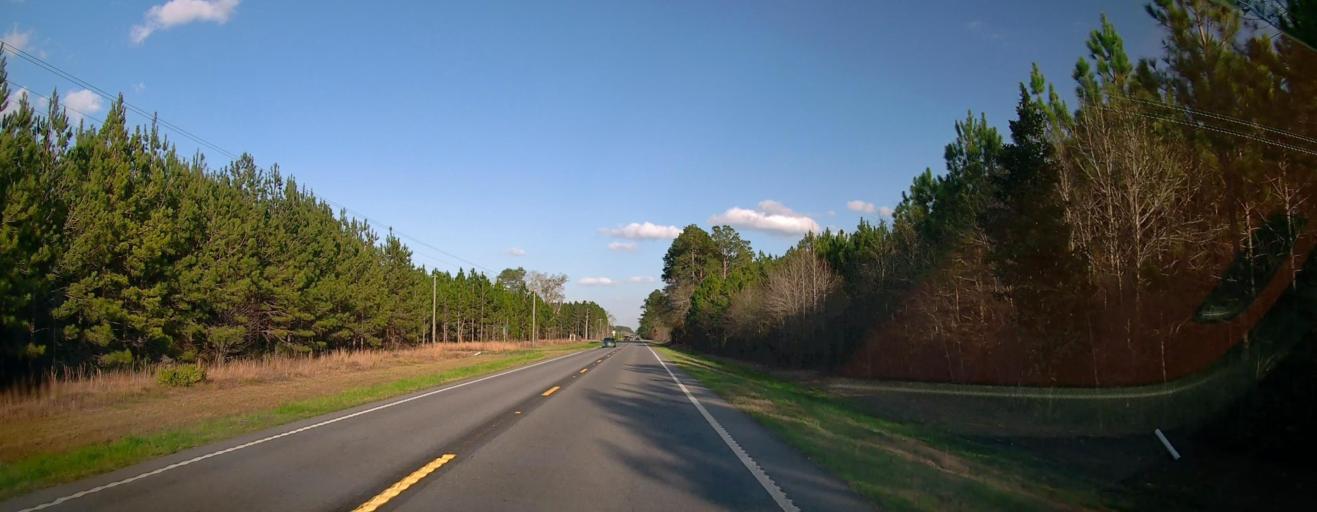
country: US
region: Georgia
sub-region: Evans County
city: Claxton
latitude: 32.1499
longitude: -82.0102
